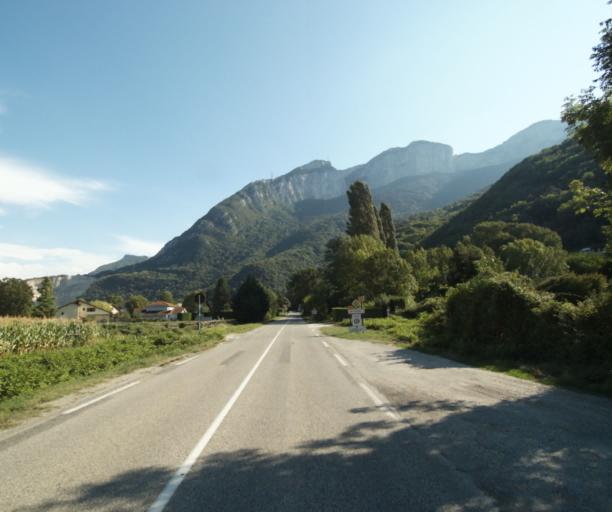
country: FR
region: Rhone-Alpes
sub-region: Departement de l'Isere
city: Noyarey
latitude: 45.2457
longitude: 5.6327
